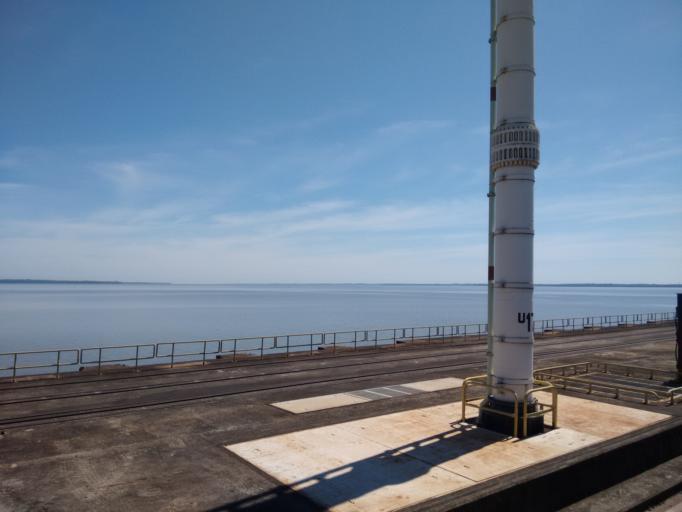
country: PY
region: Alto Parana
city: Ciudad del Este
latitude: -25.4080
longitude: -54.5857
